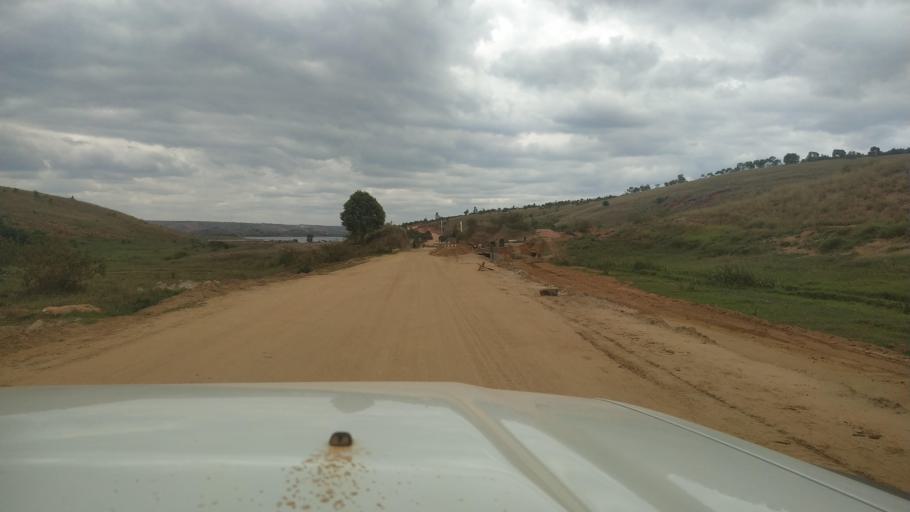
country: MG
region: Alaotra Mangoro
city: Ambatondrazaka
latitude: -17.9593
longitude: 48.2540
